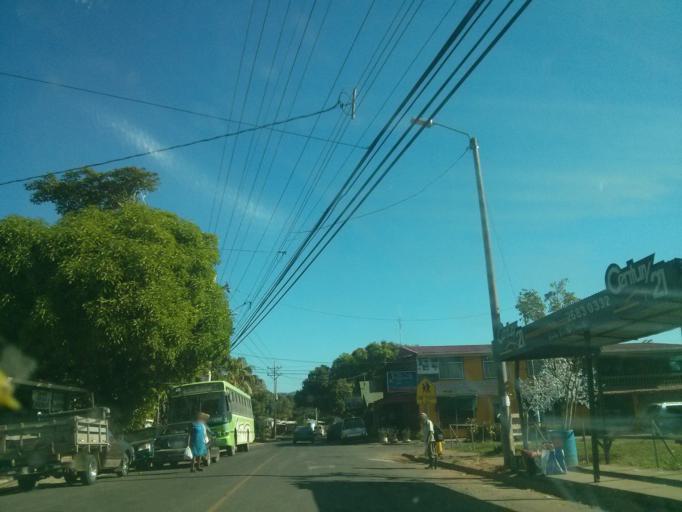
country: CR
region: Puntarenas
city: Paquera
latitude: 9.6876
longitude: -85.1047
